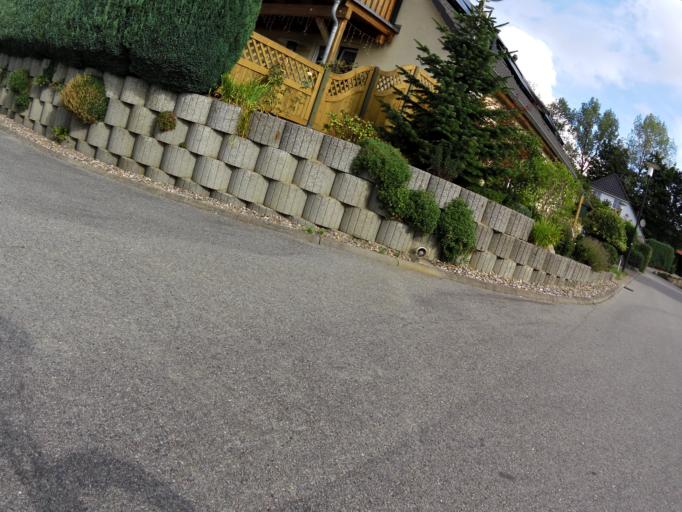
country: DE
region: Mecklenburg-Vorpommern
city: Seebad Bansin
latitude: 53.9636
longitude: 14.1281
